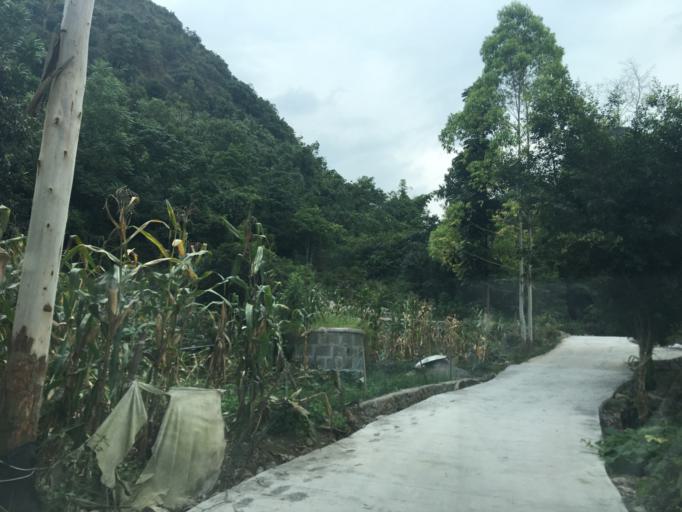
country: CN
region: Guangxi Zhuangzu Zizhiqu
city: Xinzhou
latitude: 25.2358
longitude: 105.6534
